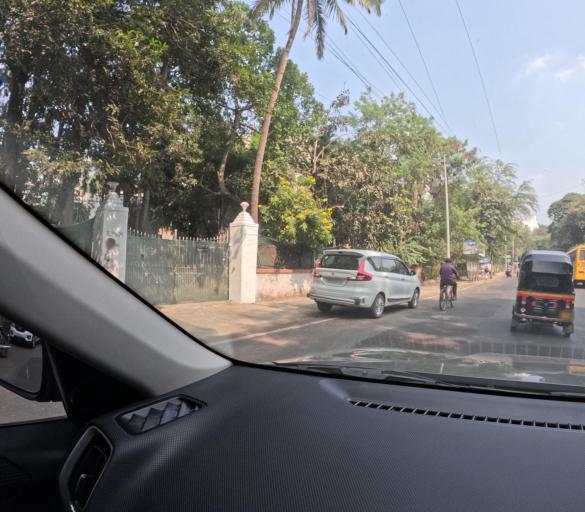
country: IN
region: Maharashtra
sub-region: Pune Division
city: Pune
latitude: 18.5248
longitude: 73.8745
